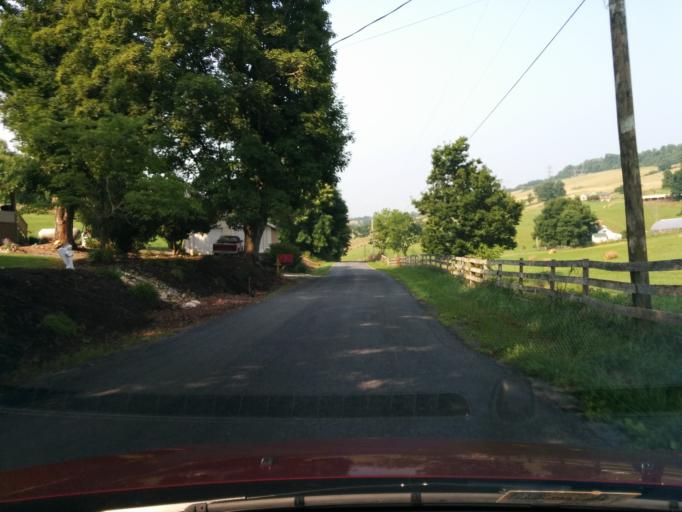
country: US
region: Virginia
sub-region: City of Lexington
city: Lexington
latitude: 37.7865
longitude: -79.5071
